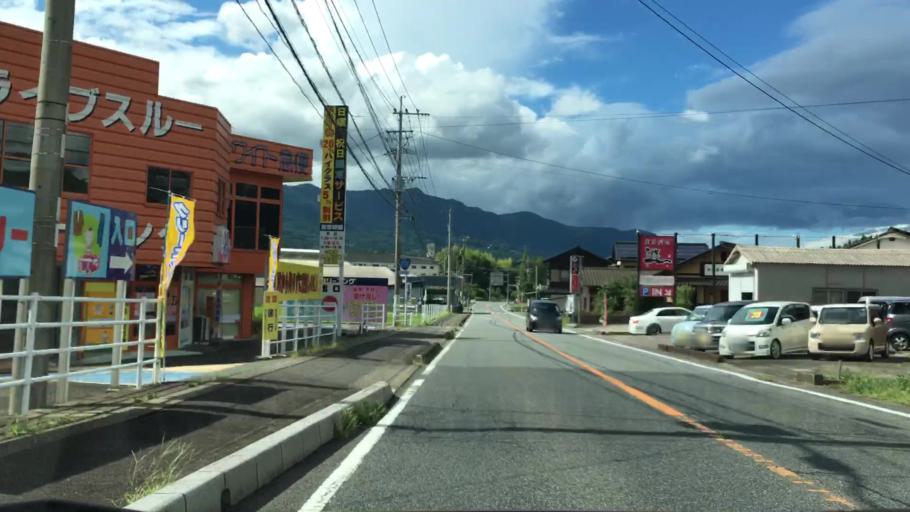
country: JP
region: Saga Prefecture
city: Imaricho-ko
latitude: 33.1856
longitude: 129.8539
